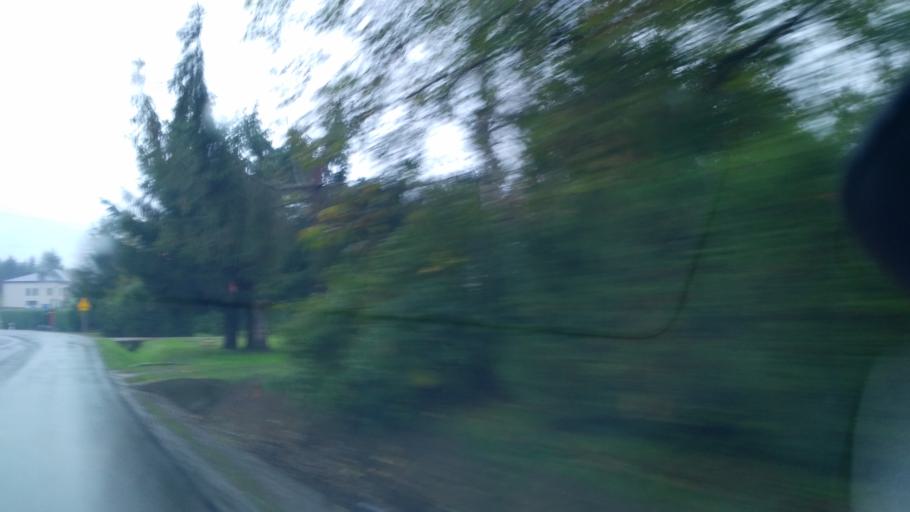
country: PL
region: Subcarpathian Voivodeship
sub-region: Powiat krosnienski
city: Korczyna
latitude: 49.7031
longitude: 21.8124
